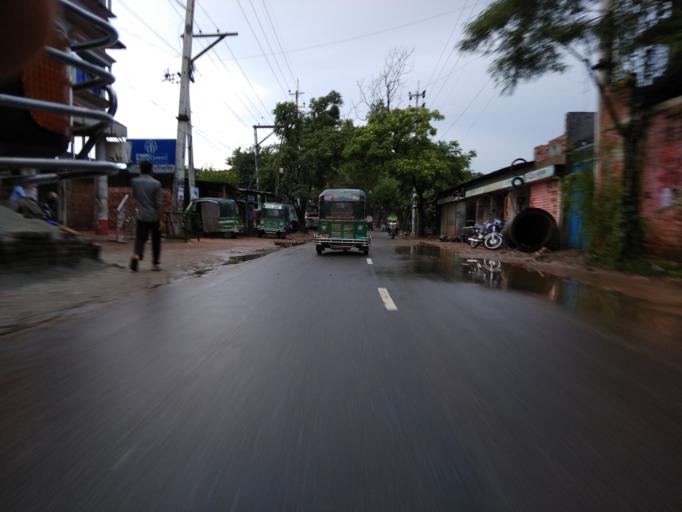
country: BD
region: Dhaka
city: Azimpur
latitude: 23.6979
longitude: 90.3424
